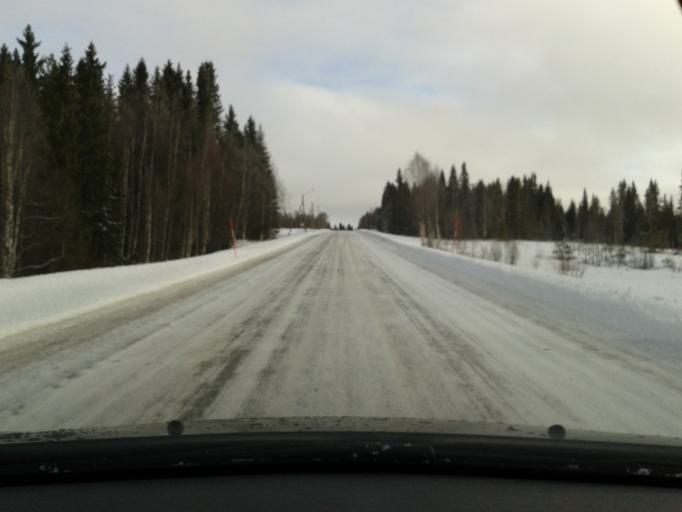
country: SE
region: Vaesterbotten
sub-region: Vilhelmina Kommun
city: Sjoberg
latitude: 64.7952
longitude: 16.0642
